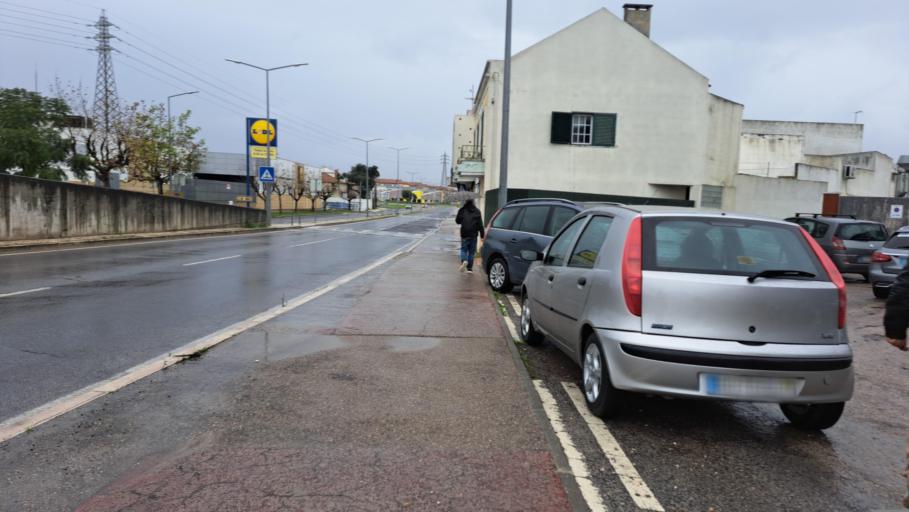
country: PT
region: Setubal
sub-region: Moita
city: Alhos Vedros
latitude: 38.6565
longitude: -9.0356
